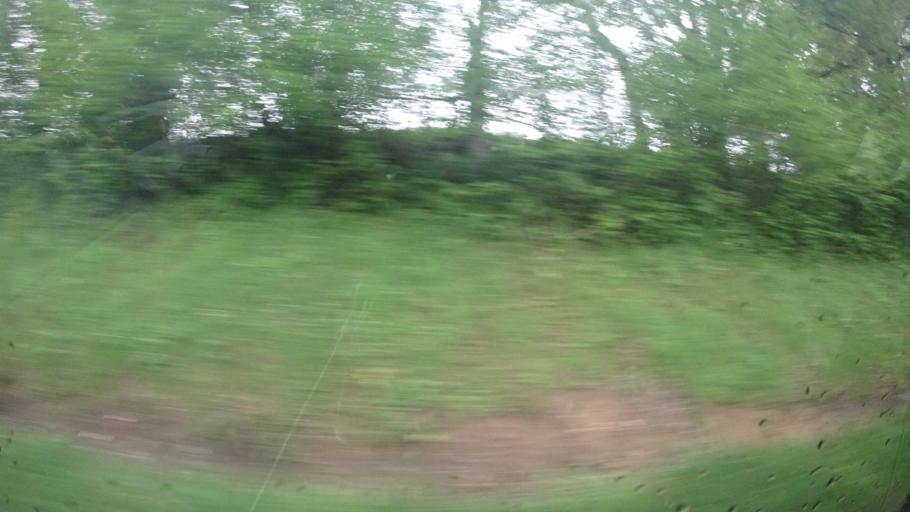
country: FR
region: Midi-Pyrenees
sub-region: Departement de l'Aveyron
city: Laissac
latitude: 44.3221
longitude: 2.7953
